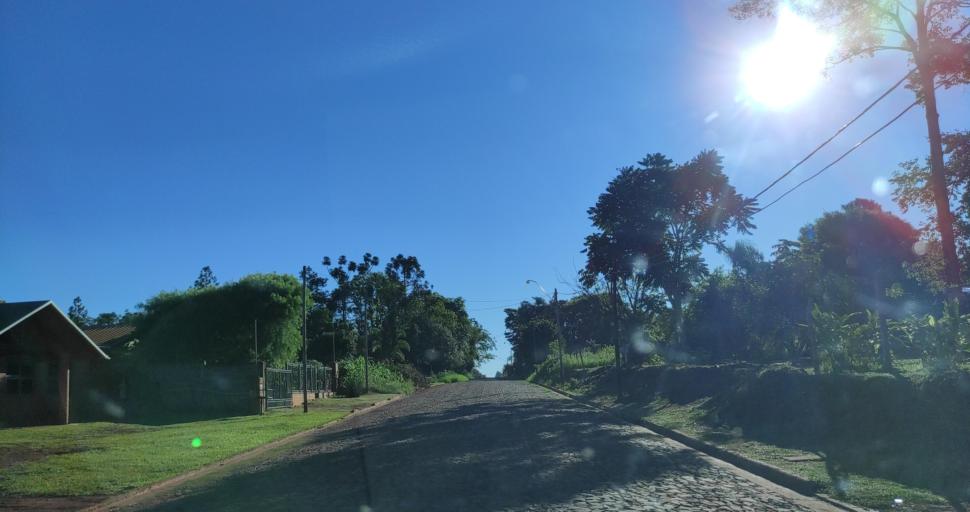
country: AR
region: Misiones
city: Puerto Rico
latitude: -26.8252
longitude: -55.0050
